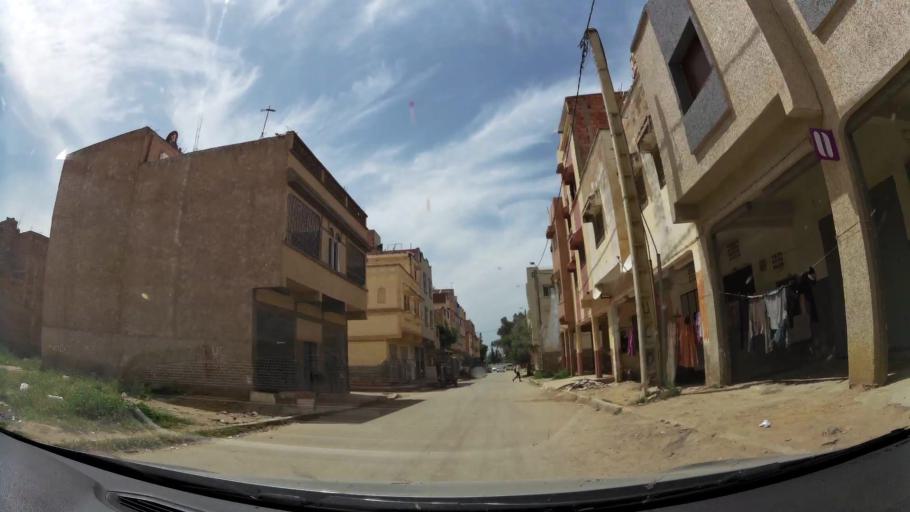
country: MA
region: Rabat-Sale-Zemmour-Zaer
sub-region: Khemisset
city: Khemisset
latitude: 33.8166
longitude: -6.0684
